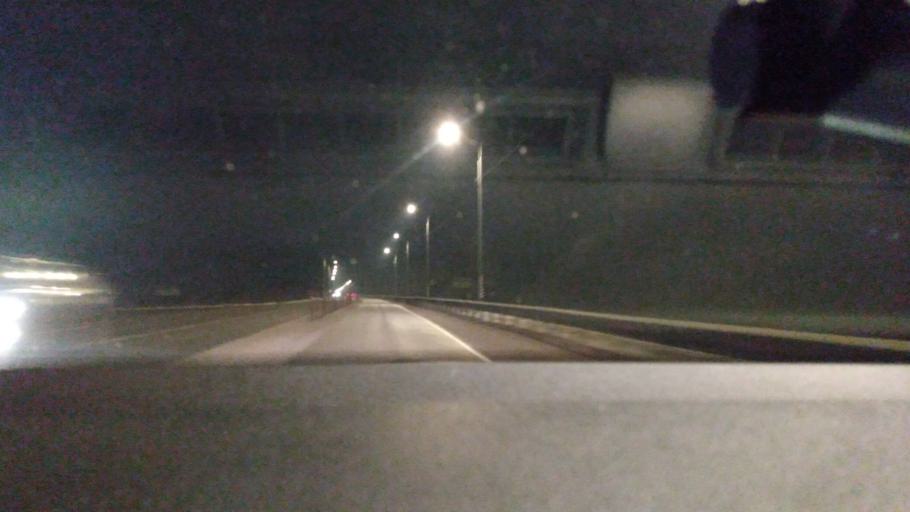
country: RU
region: Moskovskaya
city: Yegor'yevsk
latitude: 55.4478
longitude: 39.0101
